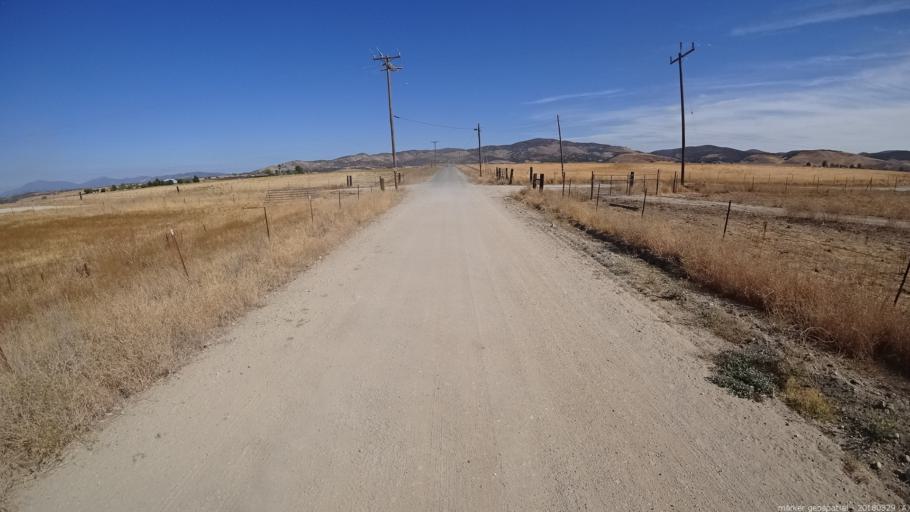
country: US
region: California
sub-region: Monterey County
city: King City
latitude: 35.9585
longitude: -121.0997
